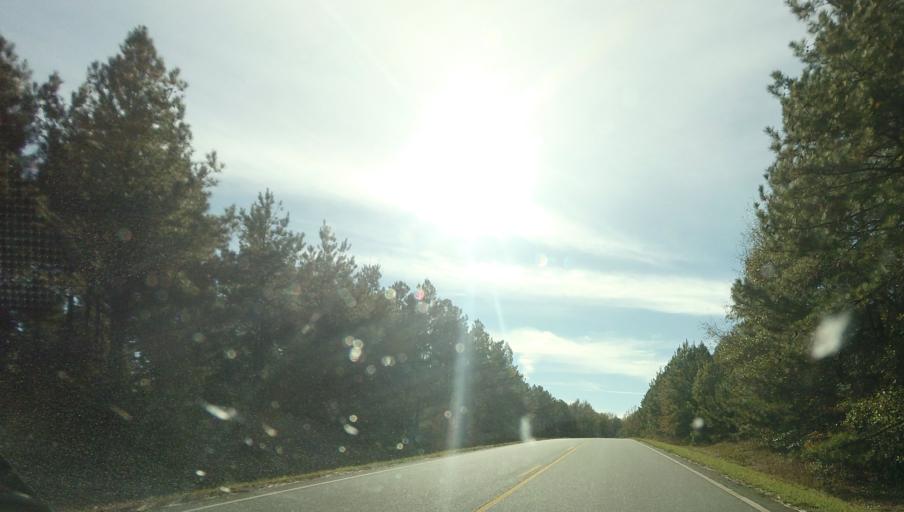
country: US
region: Georgia
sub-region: Talbot County
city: Talbotton
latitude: 32.7078
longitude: -84.3842
